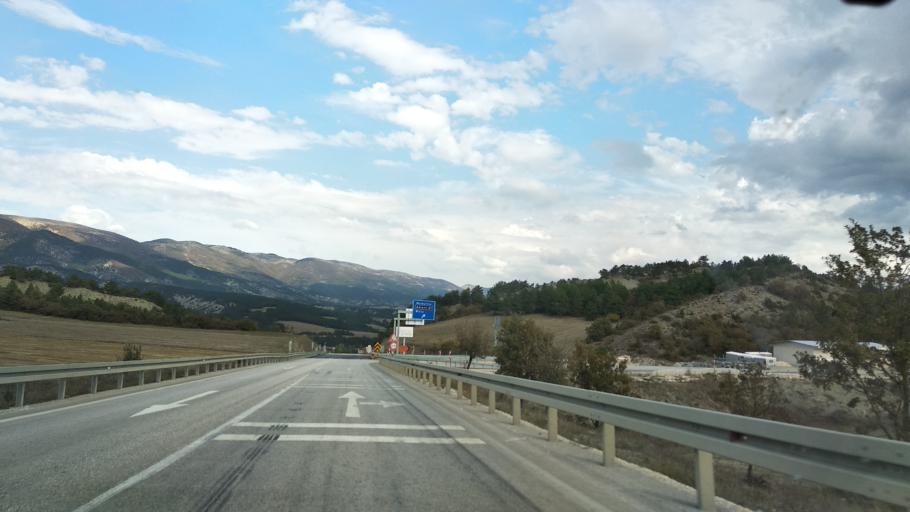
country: TR
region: Bolu
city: Mudurnu
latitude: 40.4781
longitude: 31.1576
